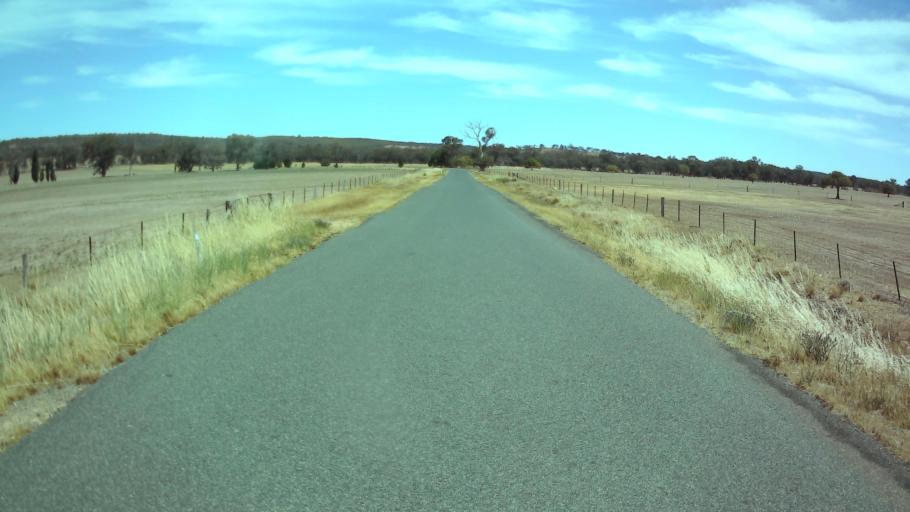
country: AU
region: New South Wales
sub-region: Weddin
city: Grenfell
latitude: -33.8397
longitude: 148.1772
